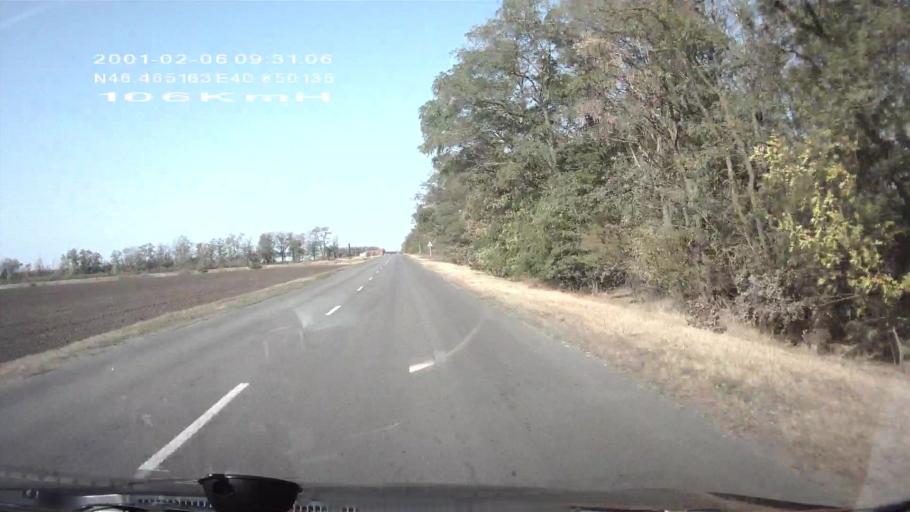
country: RU
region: Rostov
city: Tselina
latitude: 46.4651
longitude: 40.8490
